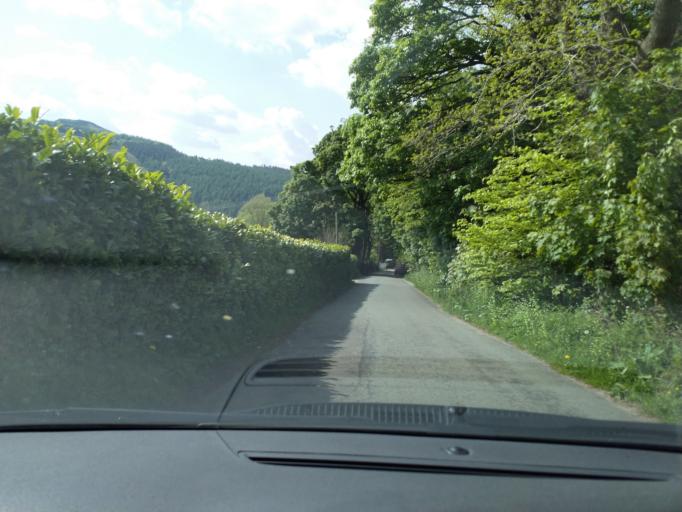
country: GB
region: England
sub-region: Derbyshire
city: Hathersage
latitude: 53.3574
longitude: -1.6941
